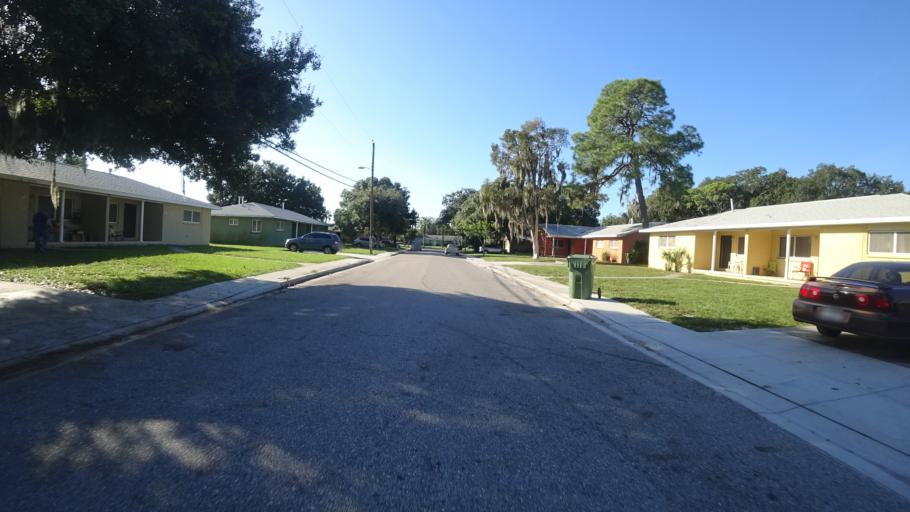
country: US
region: Florida
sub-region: Manatee County
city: Samoset
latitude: 27.4888
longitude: -82.5394
